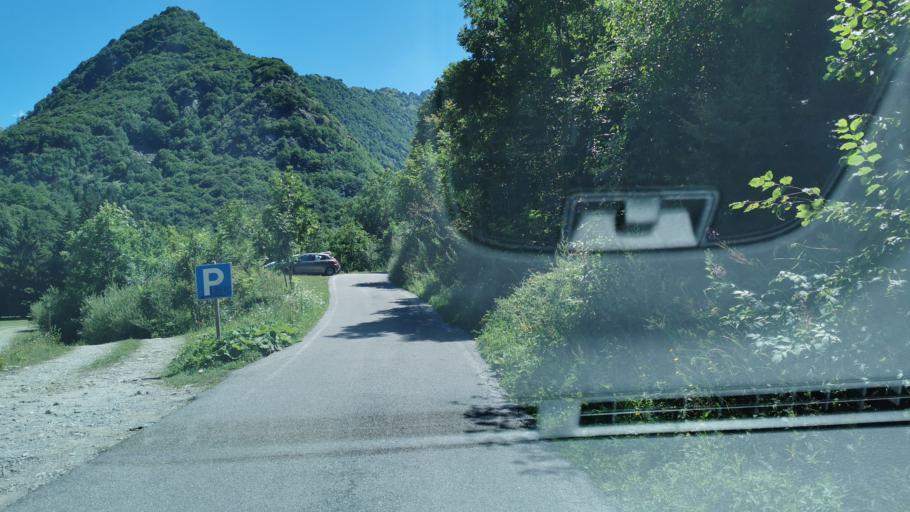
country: IT
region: Piedmont
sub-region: Provincia di Cuneo
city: Entracque
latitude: 44.1787
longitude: 7.3851
